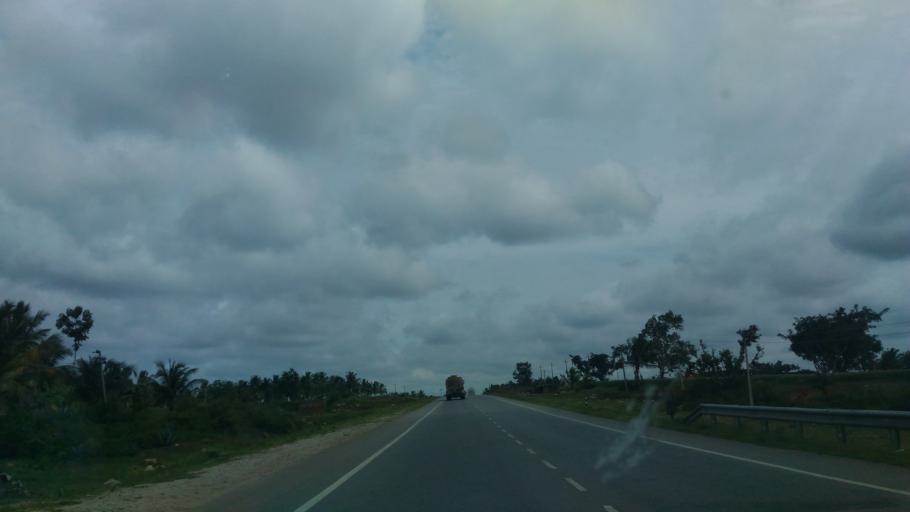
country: IN
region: Karnataka
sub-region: Hassan
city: Channarayapatna
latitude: 12.9107
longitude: 76.4194
